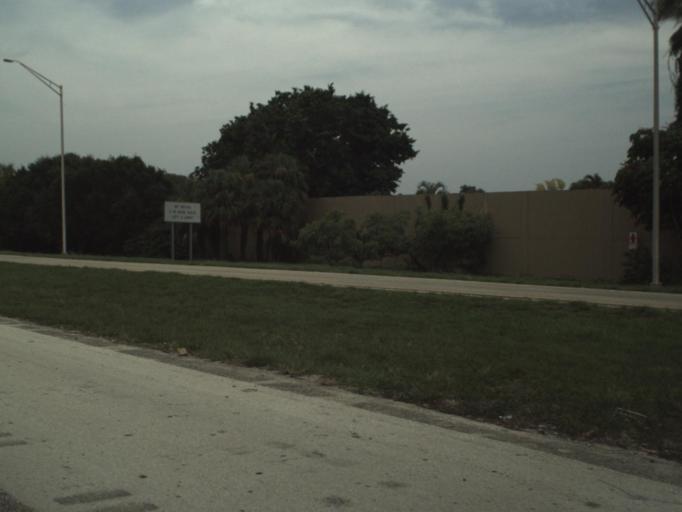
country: US
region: Florida
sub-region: Broward County
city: Kendall Green
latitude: 26.2627
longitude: -80.1310
